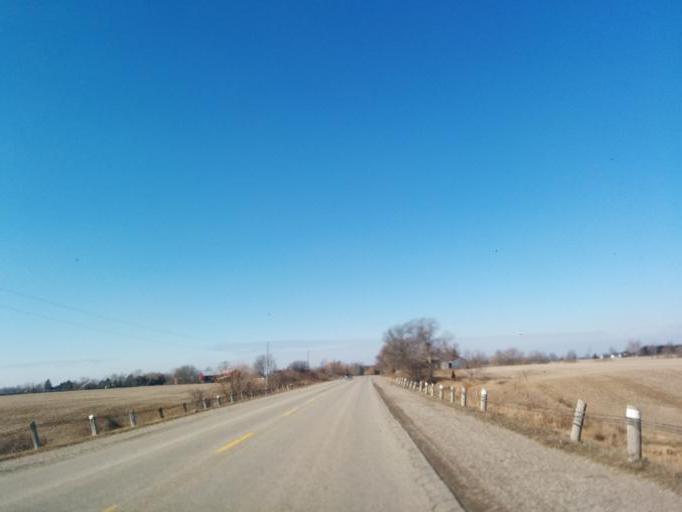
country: CA
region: Ontario
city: Brantford
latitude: 43.0394
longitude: -80.2640
